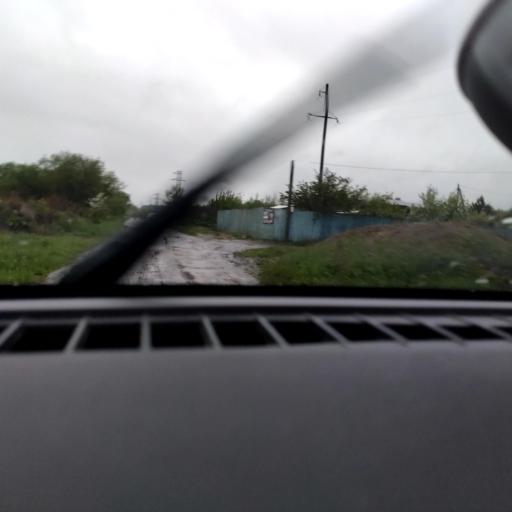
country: RU
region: Perm
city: Kondratovo
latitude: 57.9853
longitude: 56.0762
